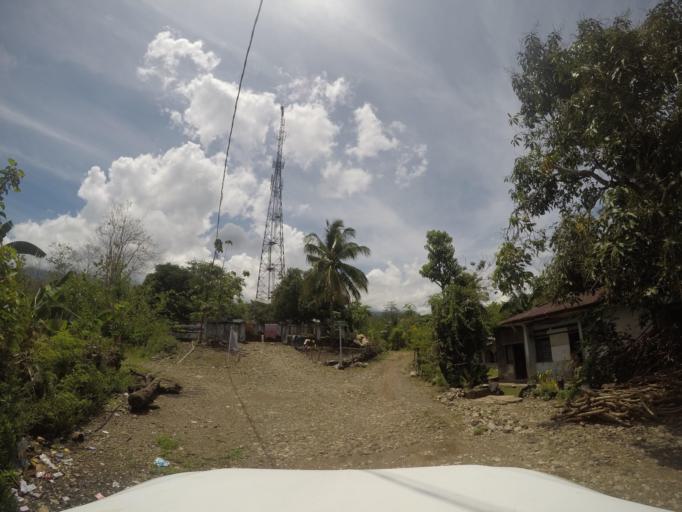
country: TL
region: Bobonaro
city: Maliana
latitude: -8.9999
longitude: 125.2251
